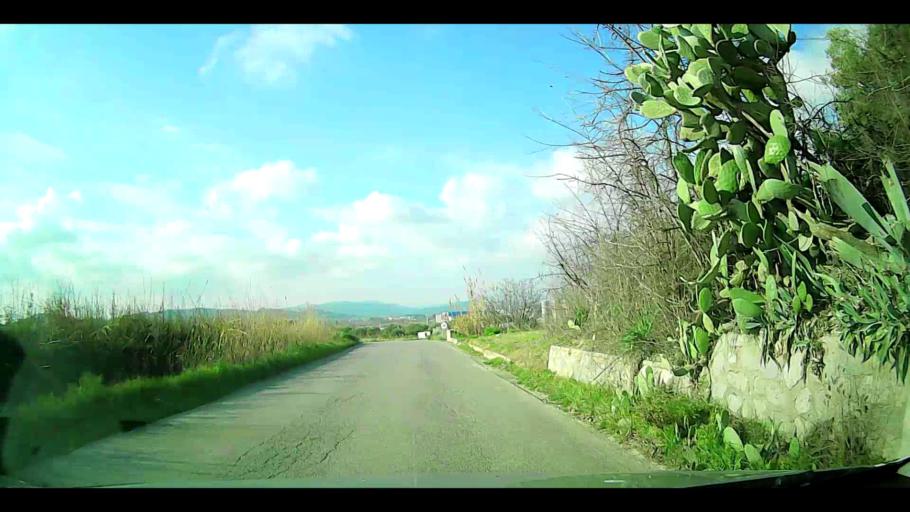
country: IT
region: Calabria
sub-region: Provincia di Crotone
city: Rocca di Neto
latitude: 39.1830
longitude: 17.0478
